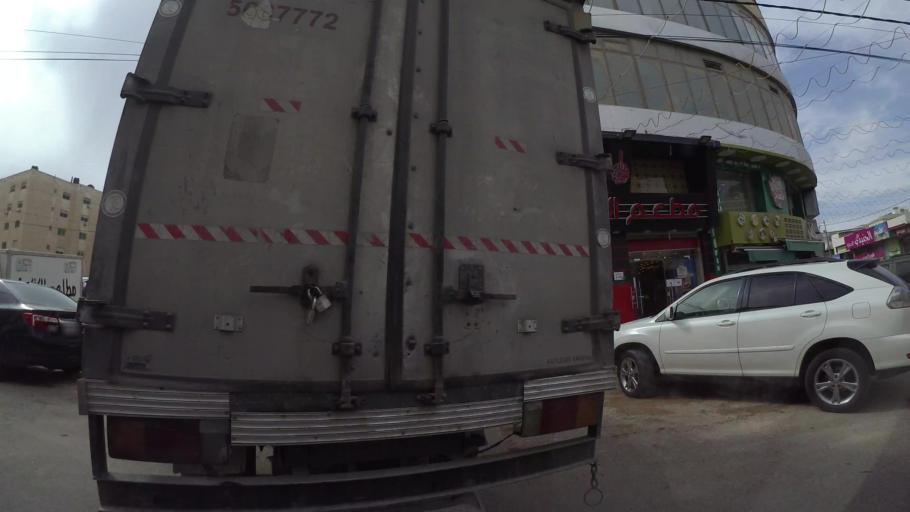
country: JO
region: Amman
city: Amman
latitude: 32.0019
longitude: 35.9411
